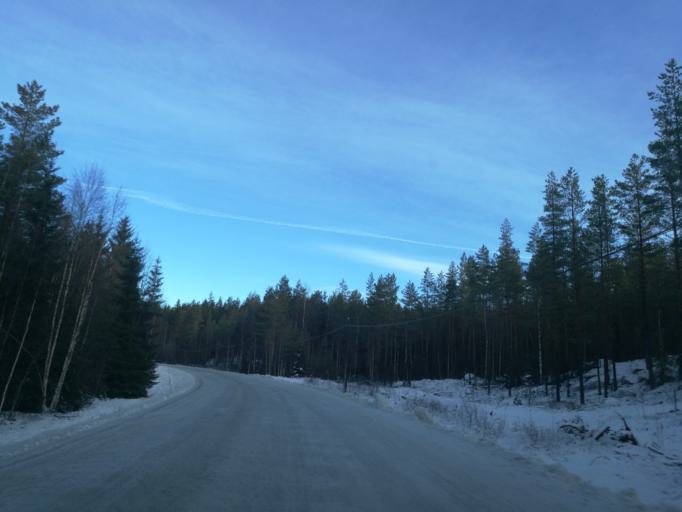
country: NO
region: Hedmark
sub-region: Grue
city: Kirkenaer
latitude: 60.3138
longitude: 12.2754
